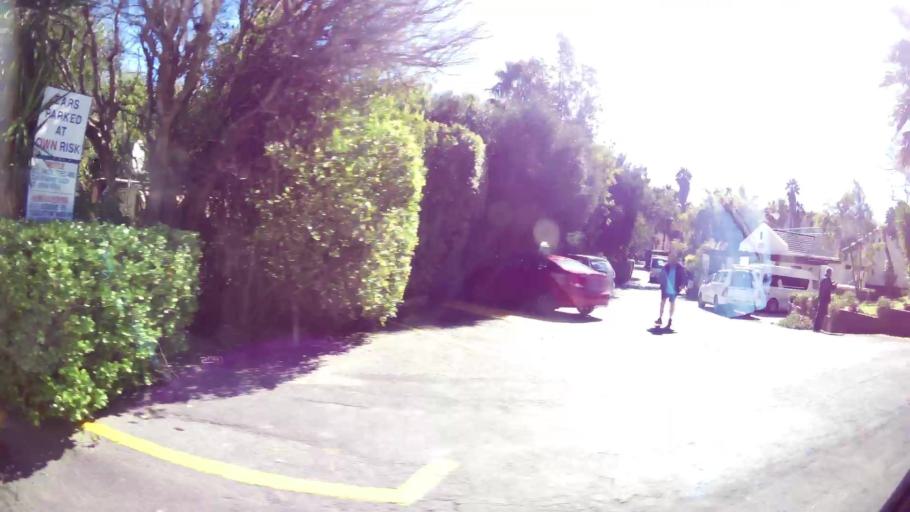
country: ZA
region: Western Cape
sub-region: Cape Winelands District Municipality
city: Ashton
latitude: -33.7650
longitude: 20.1188
